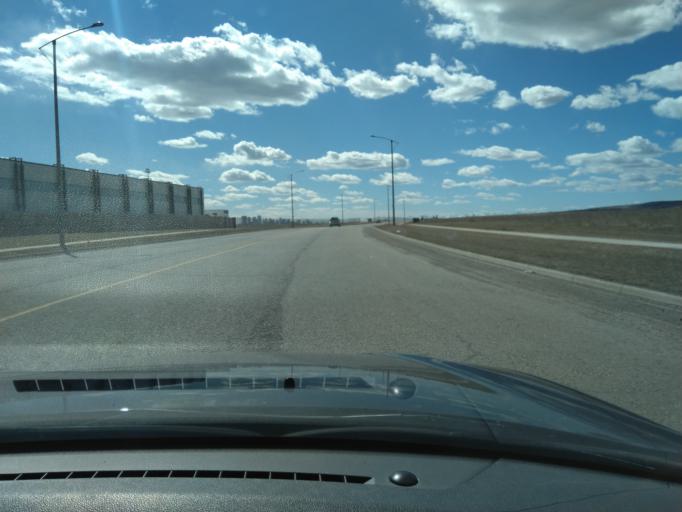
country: CA
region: Alberta
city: Calgary
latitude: 51.1331
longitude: -114.0368
